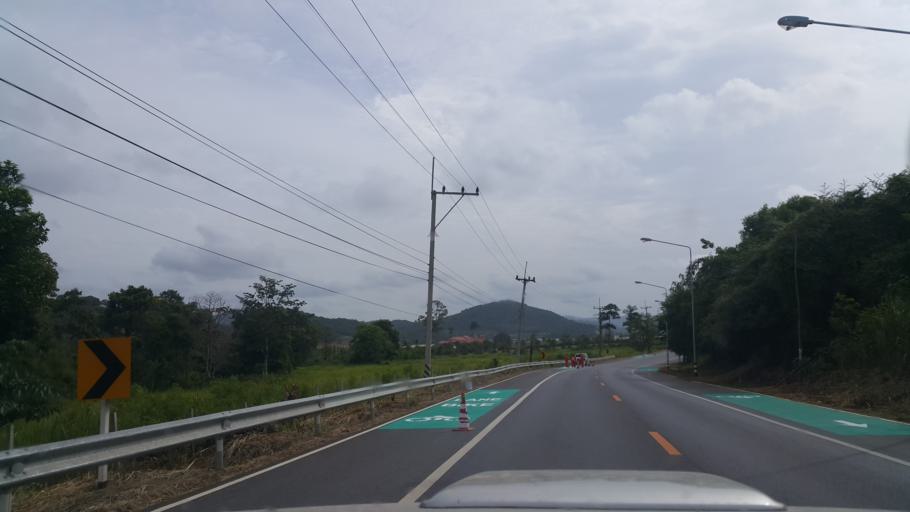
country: TH
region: Rayong
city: Ban Chang
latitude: 12.7599
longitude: 100.9720
